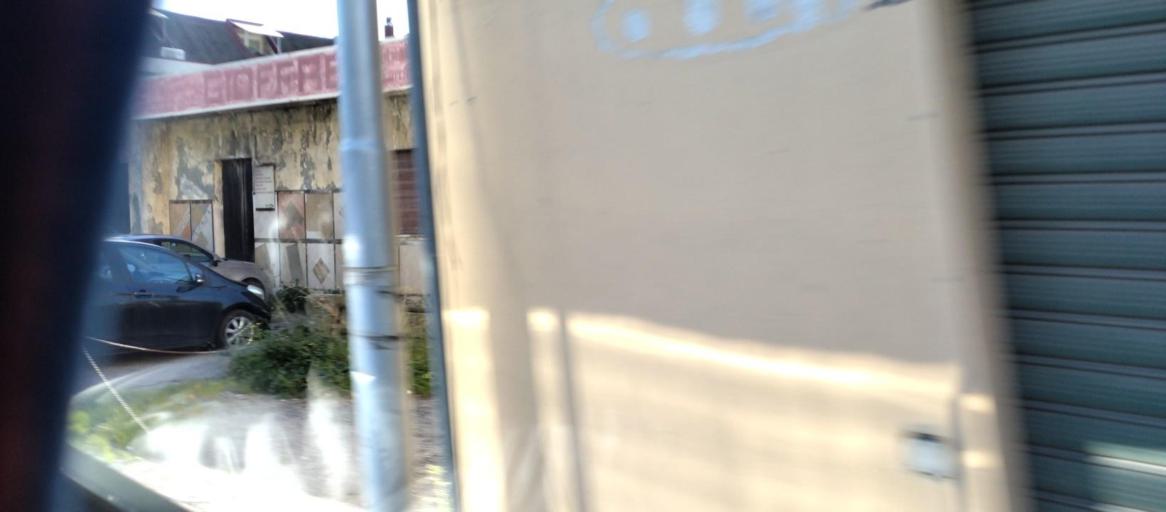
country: IT
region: Calabria
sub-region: Provincia di Catanzaro
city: Catanzaro
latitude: 38.8936
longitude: 16.6016
